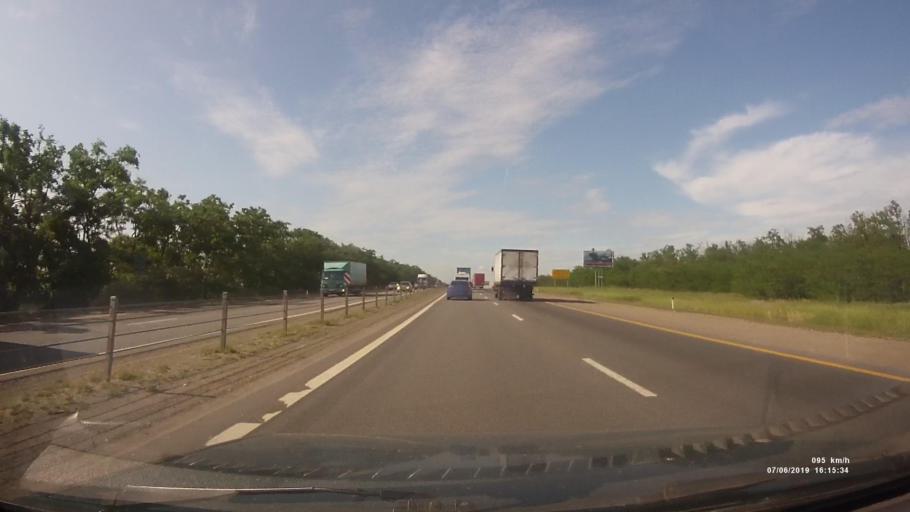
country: RU
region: Rostov
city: Likhoy
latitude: 48.1725
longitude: 40.2639
